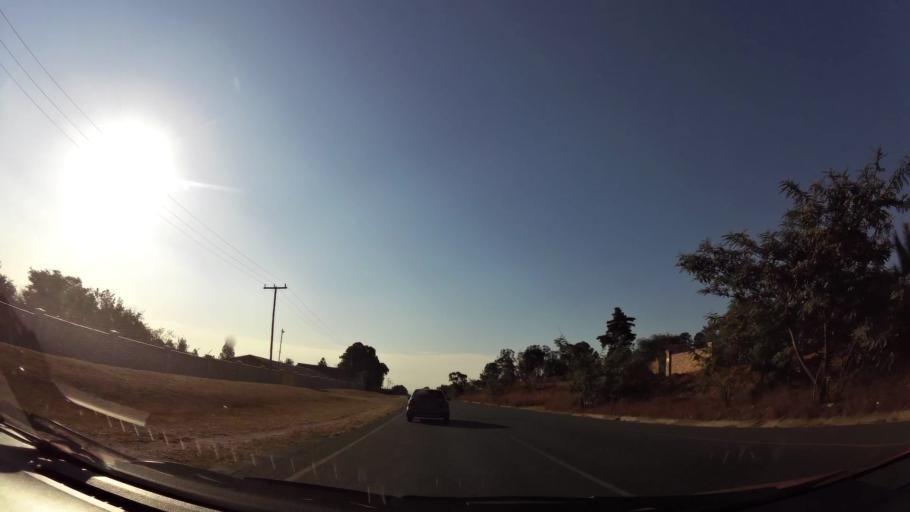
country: ZA
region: Gauteng
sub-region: West Rand District Municipality
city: Muldersdriseloop
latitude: -26.0348
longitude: 27.9096
